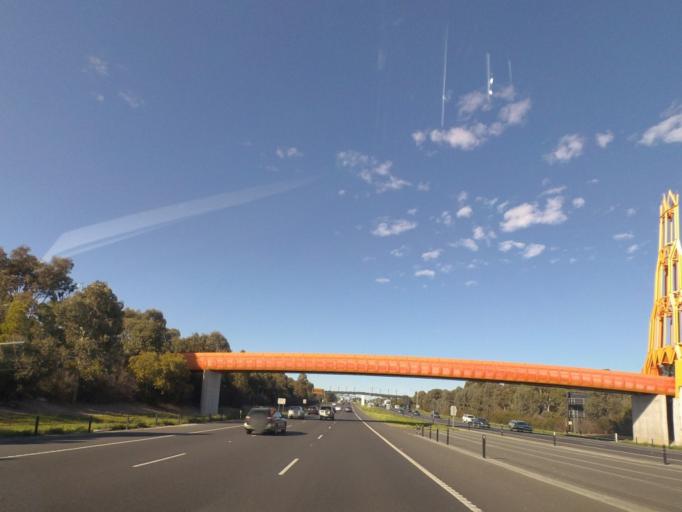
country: AU
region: Victoria
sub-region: Knox
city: Wantirna
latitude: -37.8525
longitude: 145.2151
